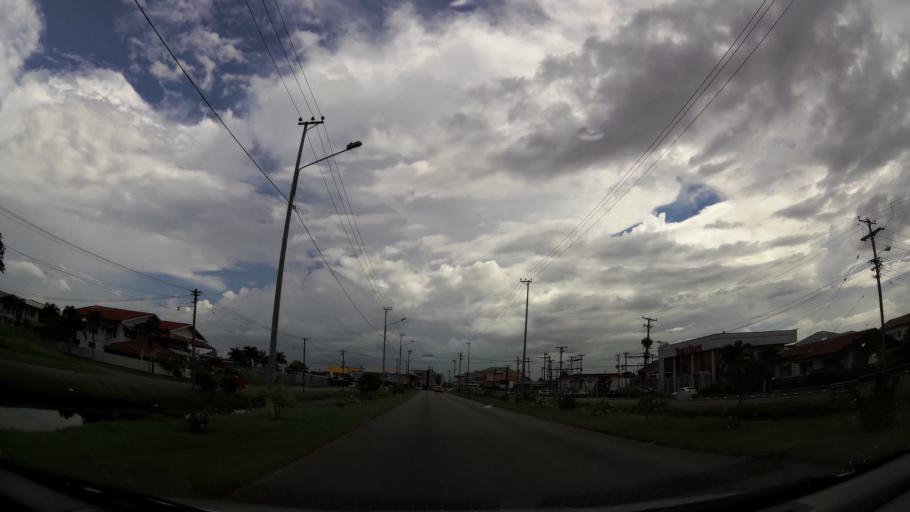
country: SR
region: Paramaribo
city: Paramaribo
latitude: 5.8419
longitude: -55.1388
